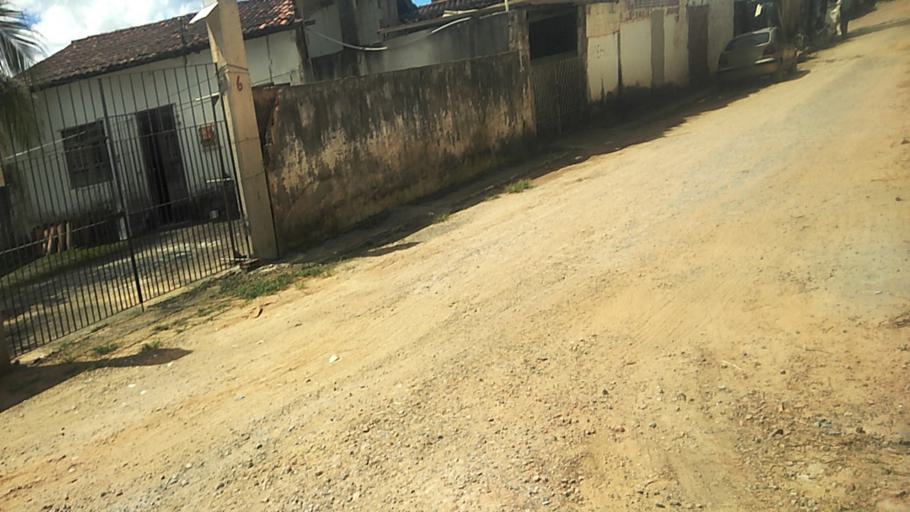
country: BR
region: Pernambuco
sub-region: Jaboatao Dos Guararapes
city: Jaboatao dos Guararapes
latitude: -8.0677
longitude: -35.0041
